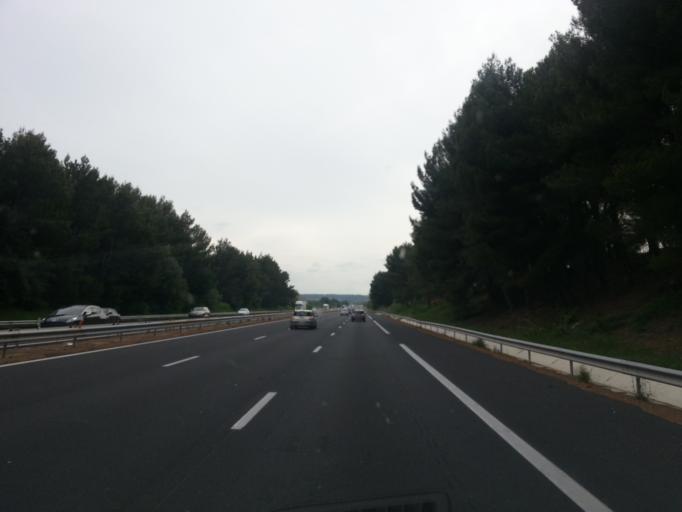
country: FR
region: Languedoc-Roussillon
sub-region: Departement du Gard
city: Remoulins
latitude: 43.9269
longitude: 4.5906
